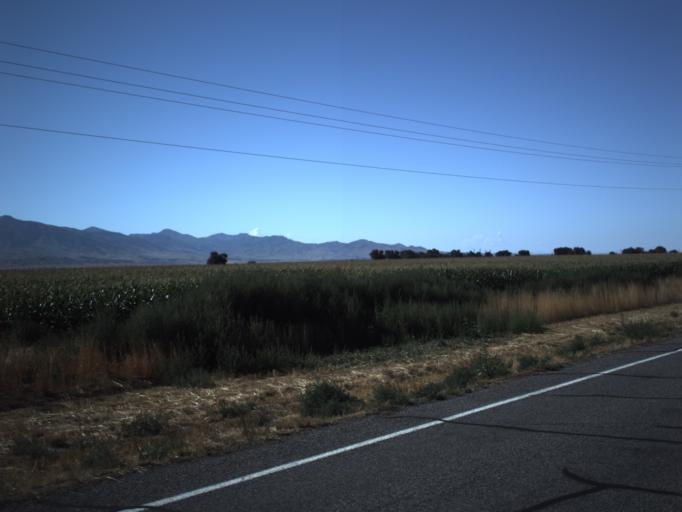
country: US
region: Utah
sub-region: Millard County
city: Delta
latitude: 39.5316
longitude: -112.3689
